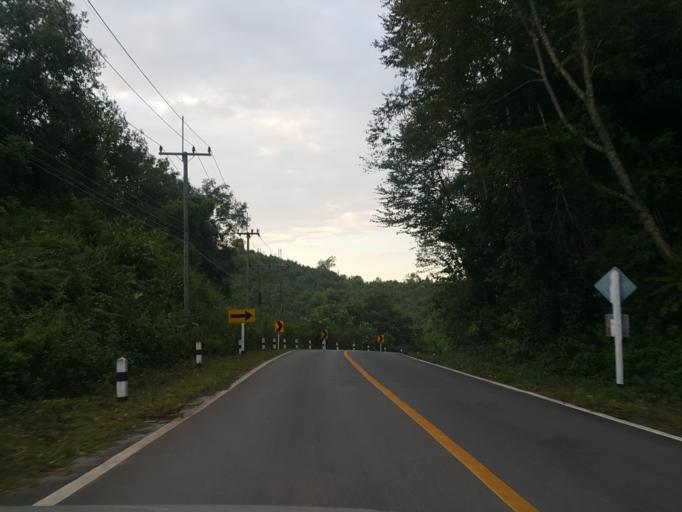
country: TH
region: Mae Hong Son
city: Khun Yuam
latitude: 18.8020
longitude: 98.0610
